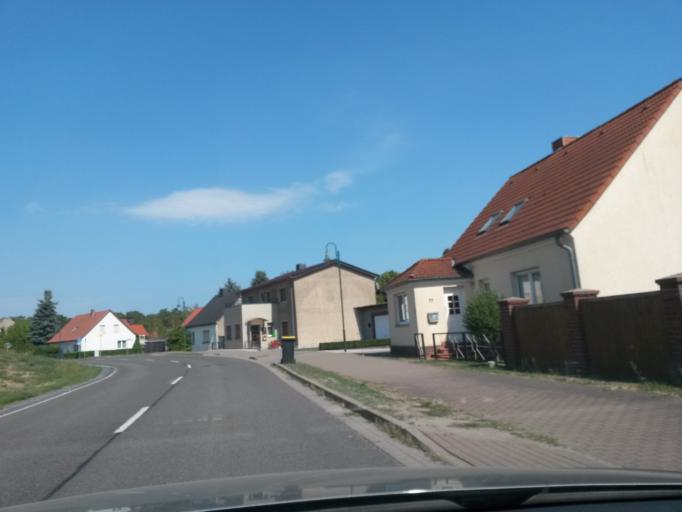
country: DE
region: Saxony-Anhalt
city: Jerichow
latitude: 52.4430
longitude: 12.0063
